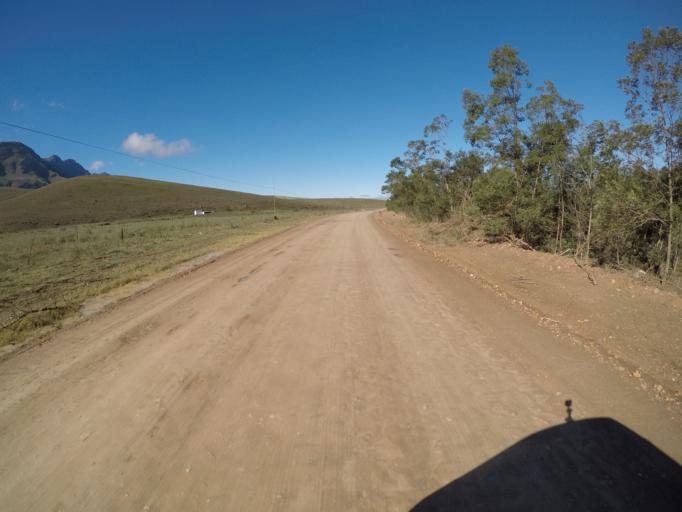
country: ZA
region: Western Cape
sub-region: Overberg District Municipality
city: Caledon
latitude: -34.0559
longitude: 19.6181
